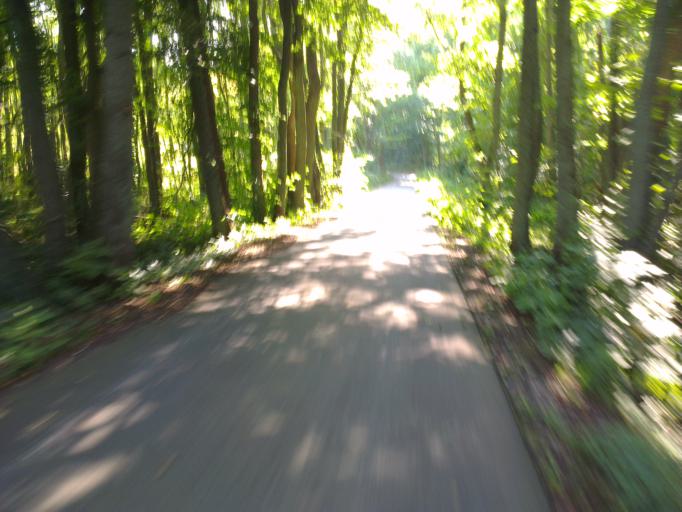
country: DK
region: Capital Region
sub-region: Frederikssund Kommune
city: Frederikssund
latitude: 55.8330
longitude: 12.0316
